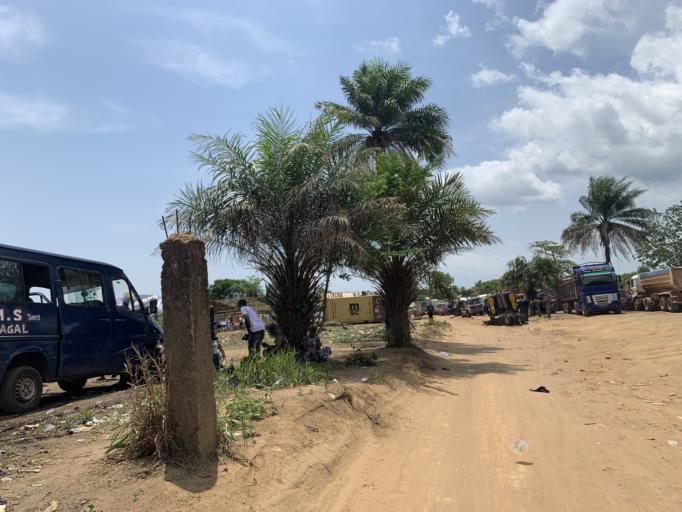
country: SL
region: Western Area
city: Waterloo
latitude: 8.3361
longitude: -13.0248
